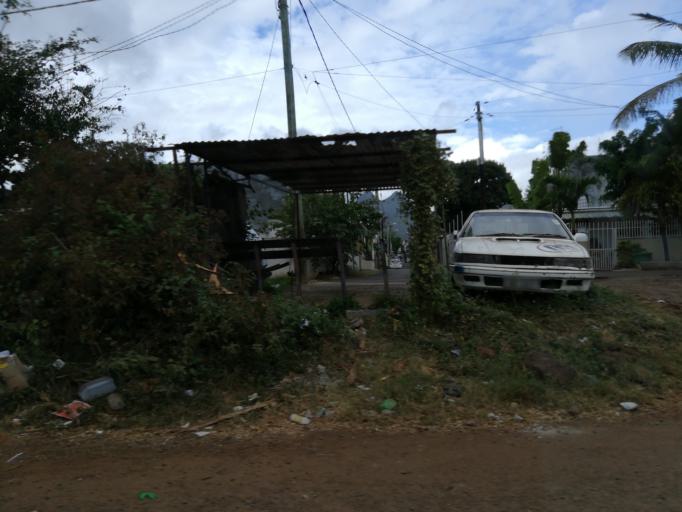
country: MU
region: Black River
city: Petite Riviere
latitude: -20.2127
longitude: 57.4646
